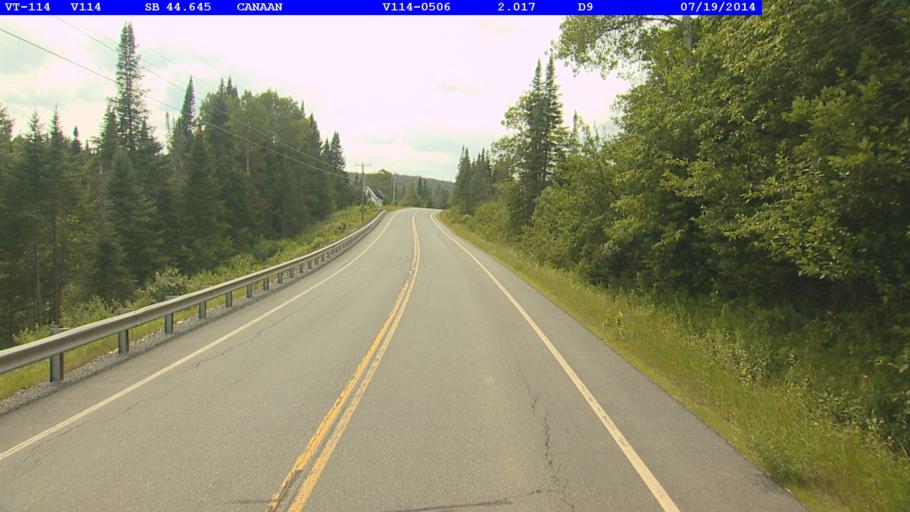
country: US
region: New Hampshire
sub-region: Coos County
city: Colebrook
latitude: 45.0059
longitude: -71.6529
